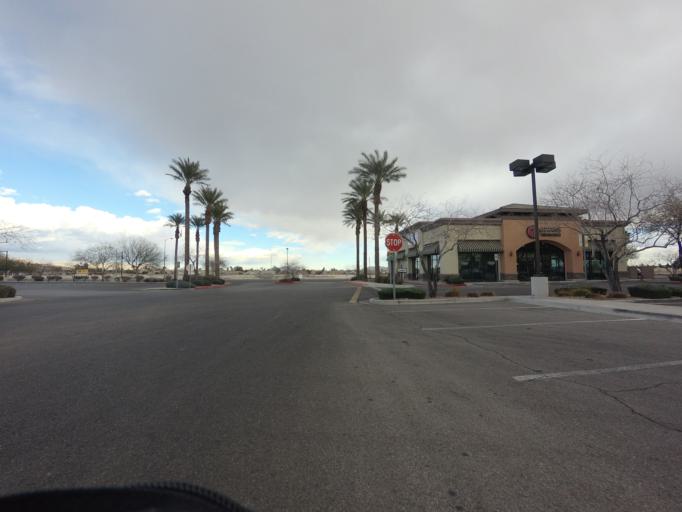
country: US
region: Nevada
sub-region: Clark County
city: North Las Vegas
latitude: 36.2598
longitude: -115.1808
